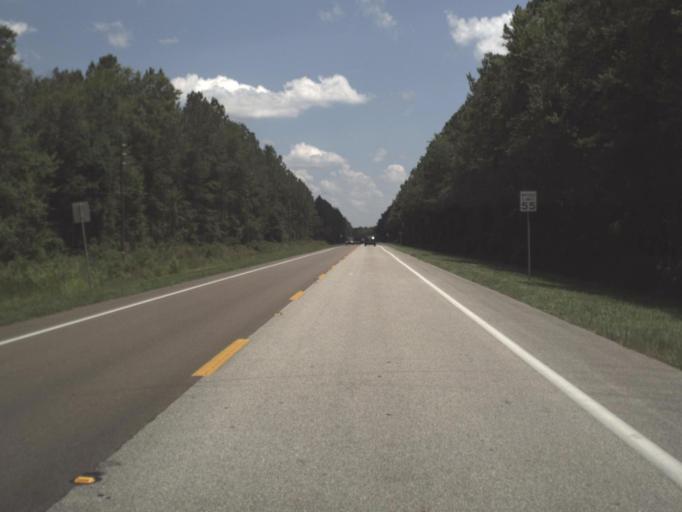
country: US
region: Florida
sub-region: Alachua County
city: Alachua
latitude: 29.7267
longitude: -82.3540
